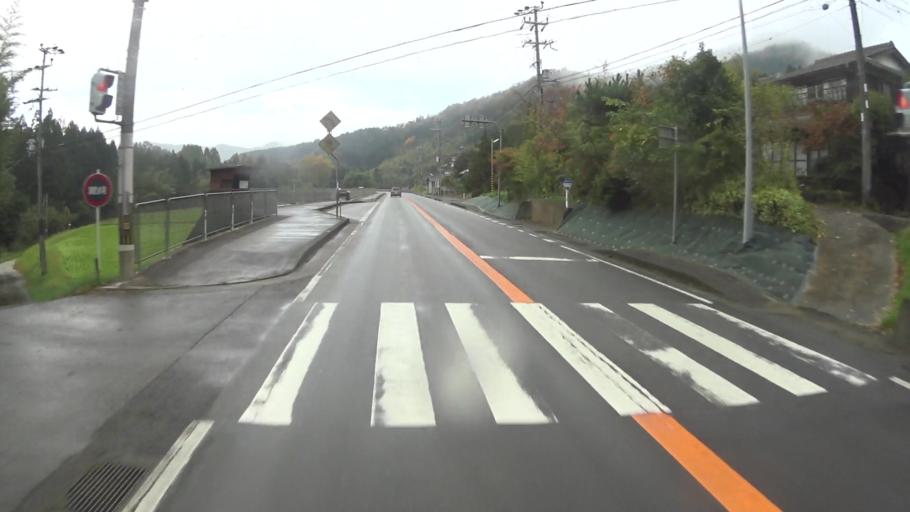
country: JP
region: Kyoto
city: Ayabe
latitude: 35.1900
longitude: 135.3052
